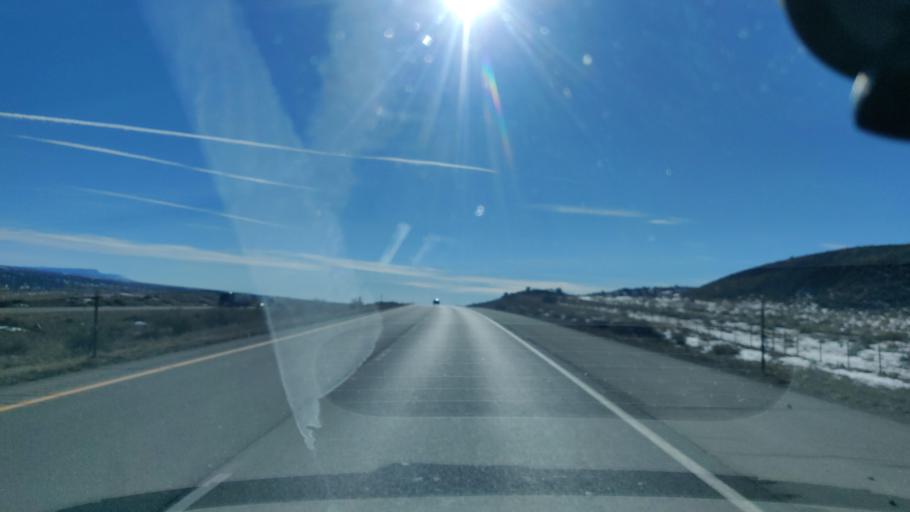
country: US
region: Colorado
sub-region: Garfield County
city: Parachute
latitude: 39.3953
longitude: -108.1269
